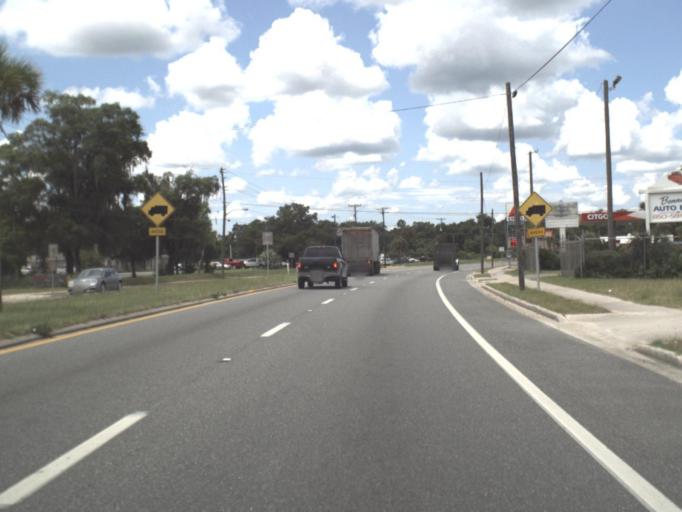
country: US
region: Florida
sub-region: Taylor County
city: Perry
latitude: 30.1036
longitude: -83.5883
